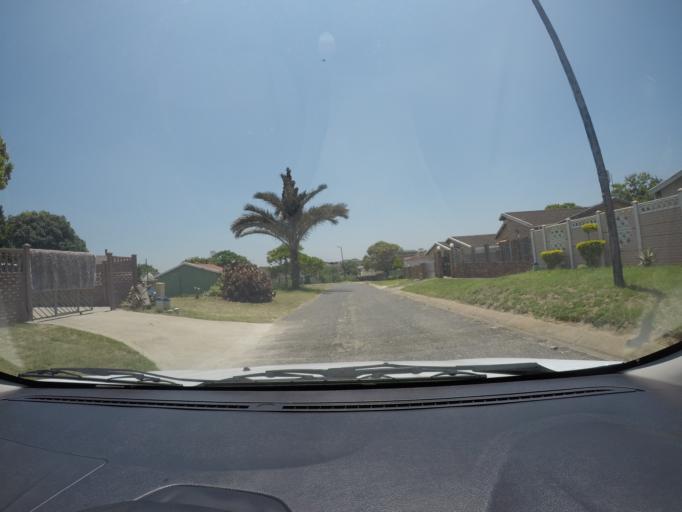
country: ZA
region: KwaZulu-Natal
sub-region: uThungulu District Municipality
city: eSikhawini
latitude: -28.8785
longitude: 31.9067
